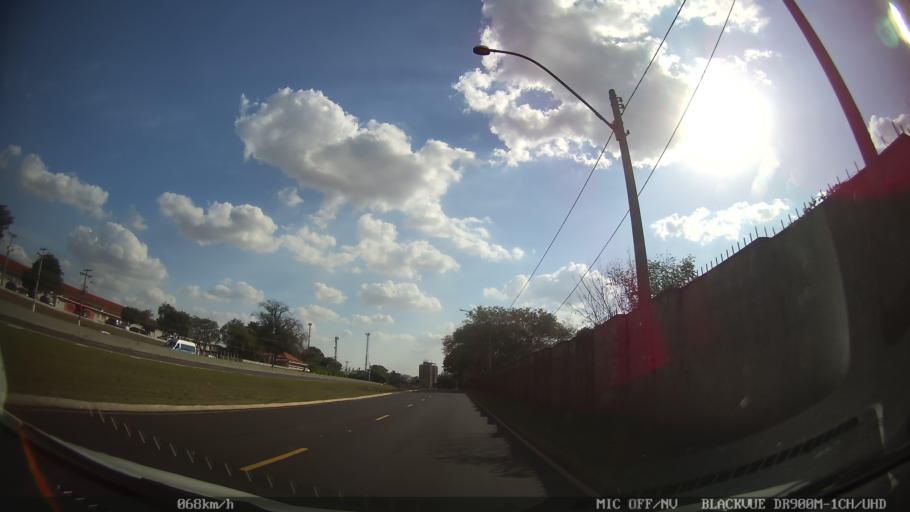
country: BR
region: Sao Paulo
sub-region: Ribeirao Preto
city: Ribeirao Preto
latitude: -21.1761
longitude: -47.8497
